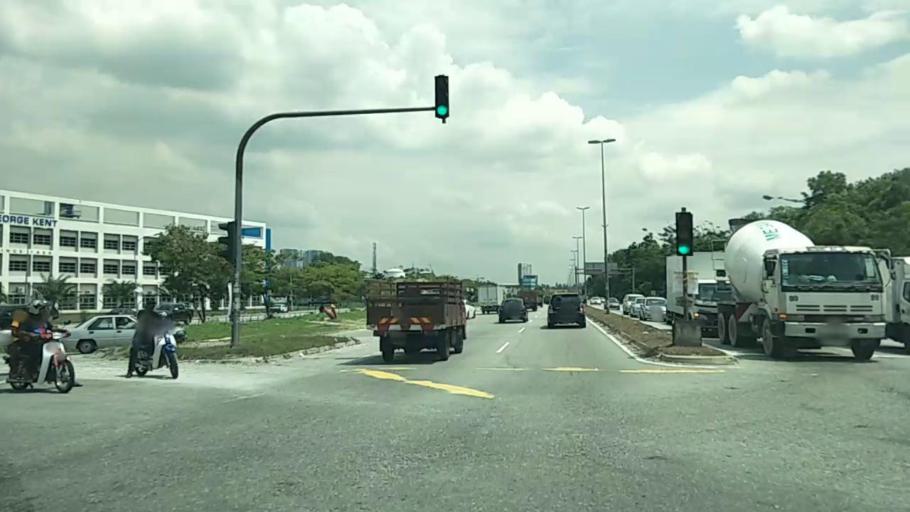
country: MY
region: Selangor
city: Subang Jaya
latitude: 2.9686
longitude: 101.6138
